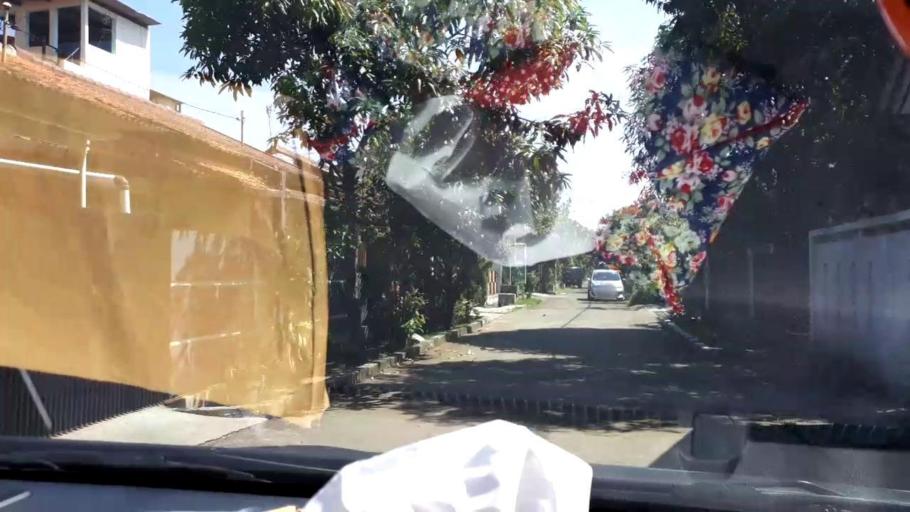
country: ID
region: West Java
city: Bandung
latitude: -6.9234
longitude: 107.6730
